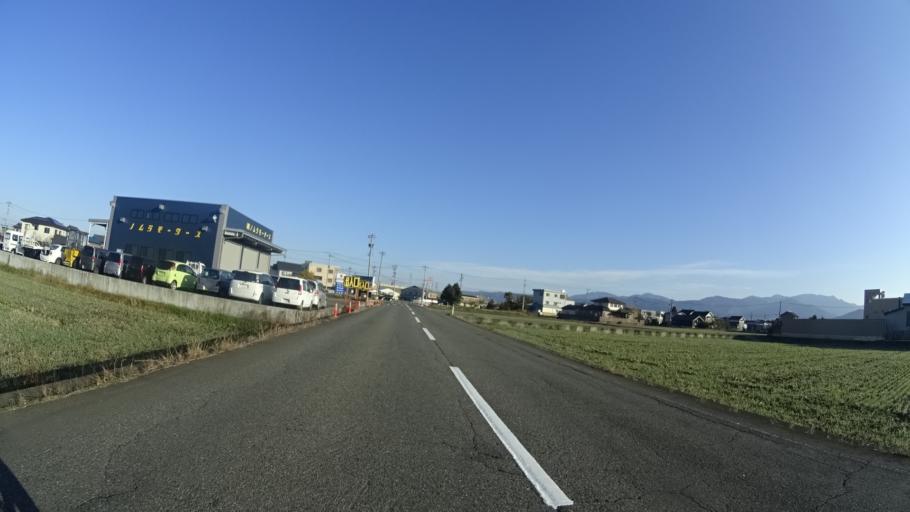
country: JP
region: Fukui
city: Fukui-shi
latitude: 36.0798
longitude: 136.2591
